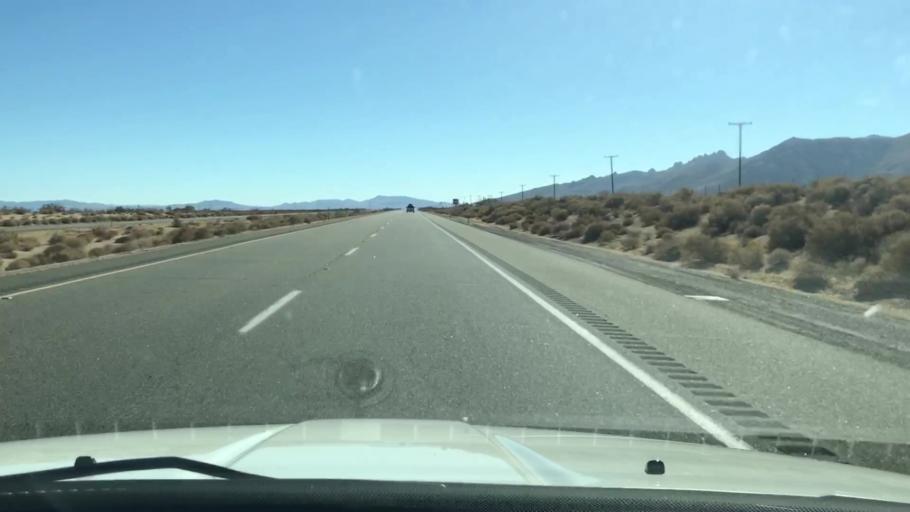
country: US
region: California
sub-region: Kern County
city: Inyokern
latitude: 35.7876
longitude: -117.8724
